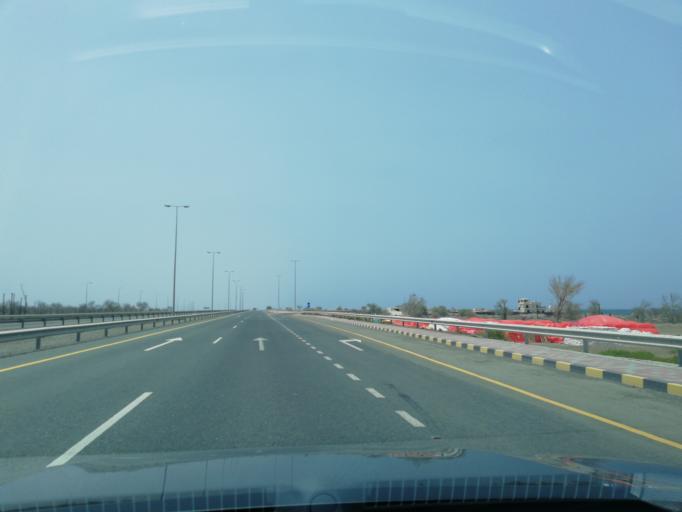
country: OM
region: Al Batinah
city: Shinas
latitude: 24.6536
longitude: 56.5140
